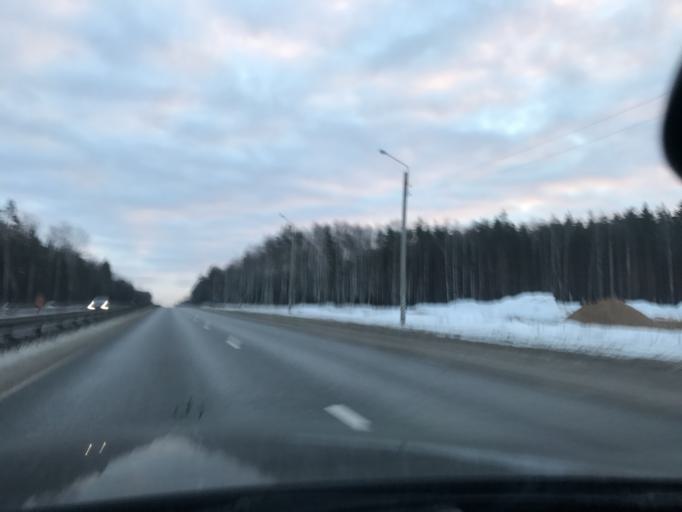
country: RU
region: Vladimir
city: Melekhovo
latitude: 56.2132
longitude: 41.3475
